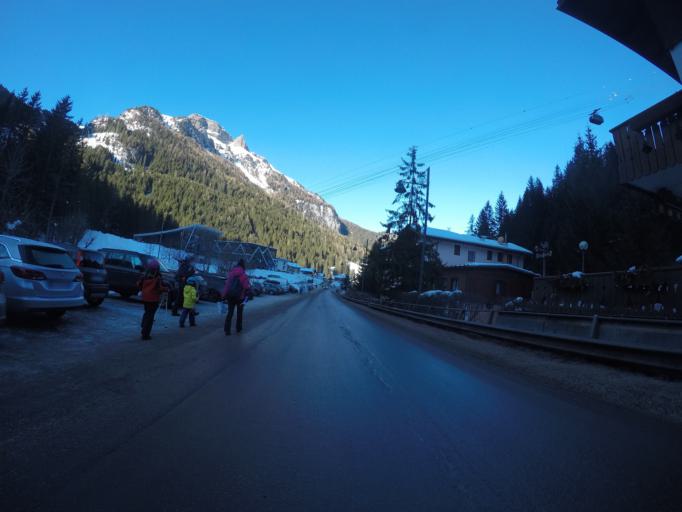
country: IT
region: Trentino-Alto Adige
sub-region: Provincia di Trento
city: Canazei
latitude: 46.4579
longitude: 11.7910
